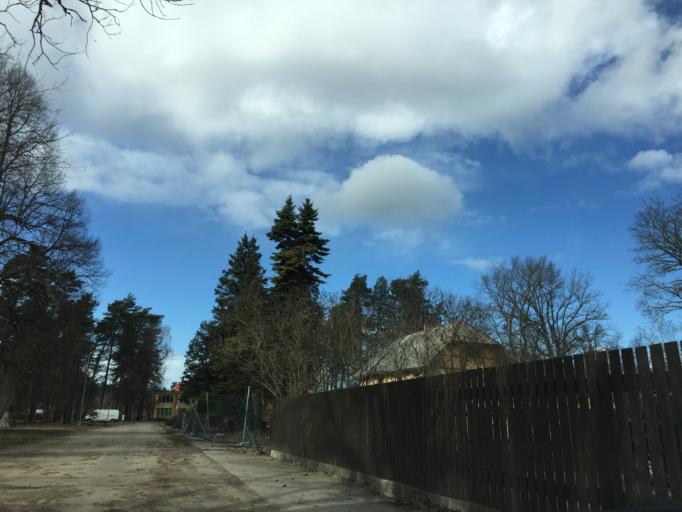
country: LV
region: Garkalne
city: Garkalne
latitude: 56.9686
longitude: 24.4892
